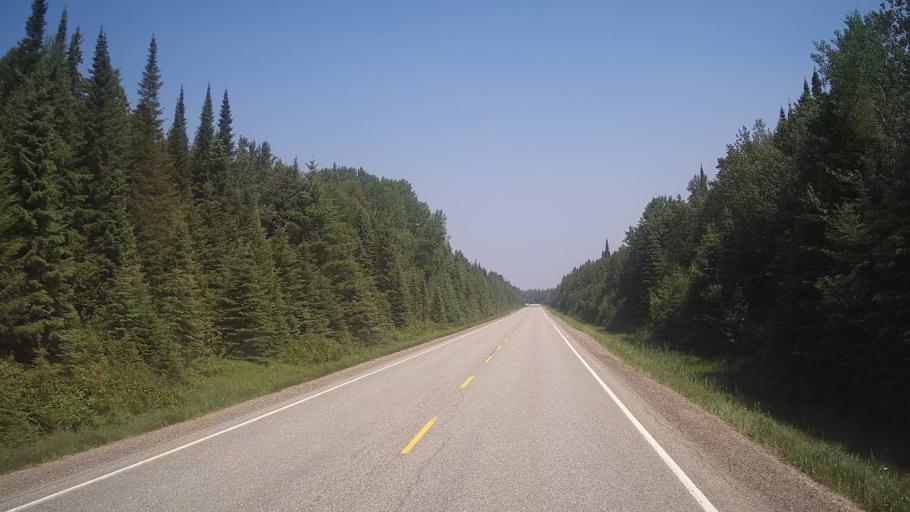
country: CA
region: Ontario
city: Timmins
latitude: 48.2081
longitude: -81.5757
